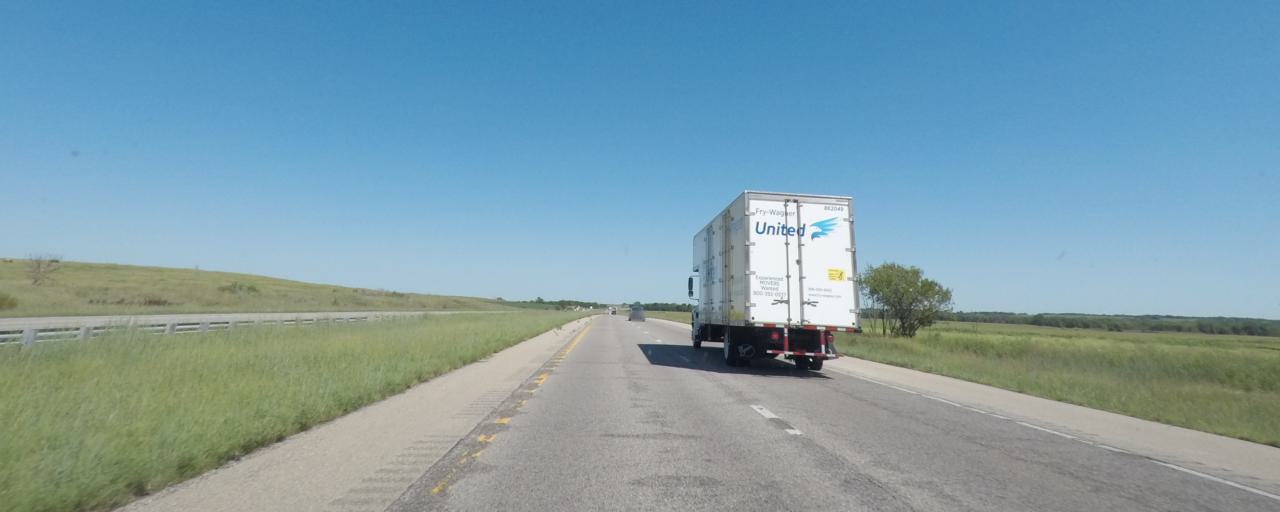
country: US
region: Kansas
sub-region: Osage County
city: Lyndon
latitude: 38.4264
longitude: -95.7843
